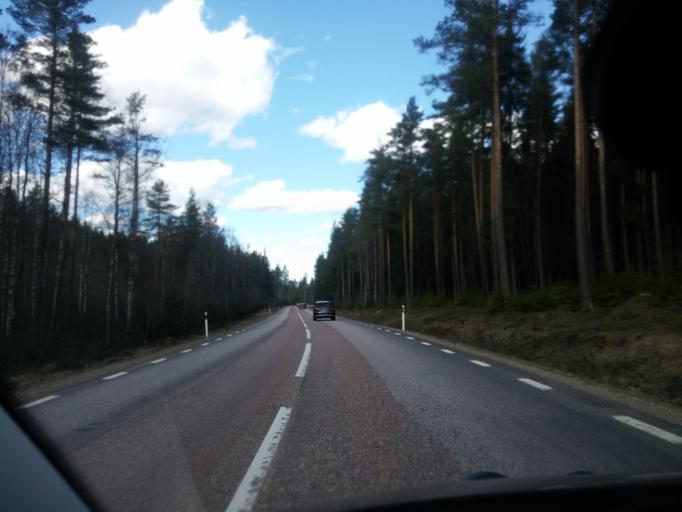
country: SE
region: Dalarna
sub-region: Faluns Kommun
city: Svardsjo
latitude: 60.7734
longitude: 15.7553
